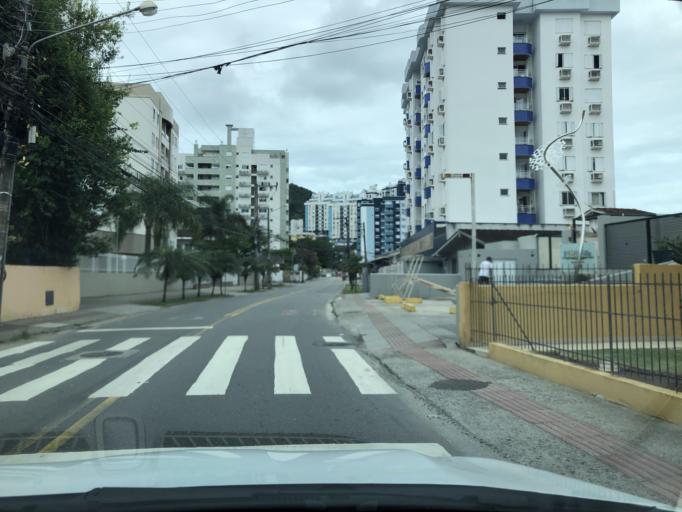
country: BR
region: Santa Catarina
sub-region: Florianopolis
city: Itacorubi
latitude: -27.5836
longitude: -48.4998
